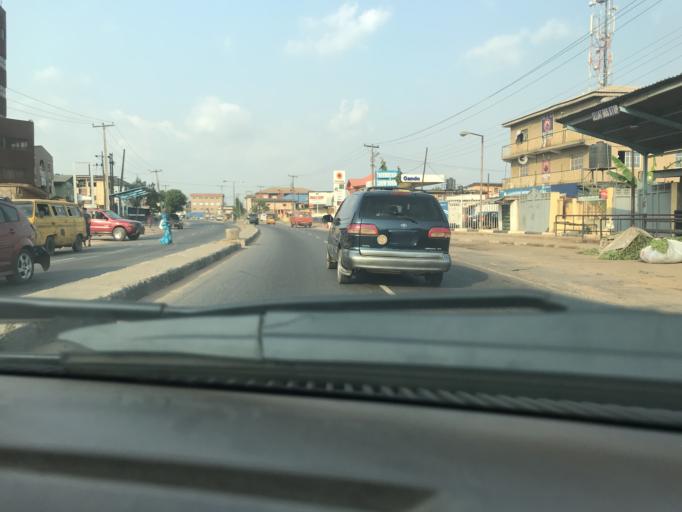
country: NG
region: Lagos
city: Agege
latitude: 6.5883
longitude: 3.2870
